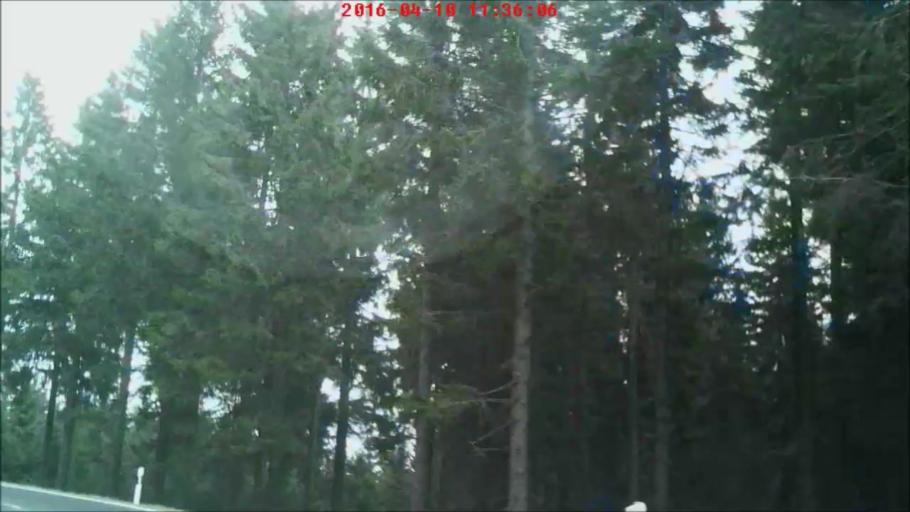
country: DE
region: Thuringia
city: Oberhof
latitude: 50.6907
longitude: 10.7293
